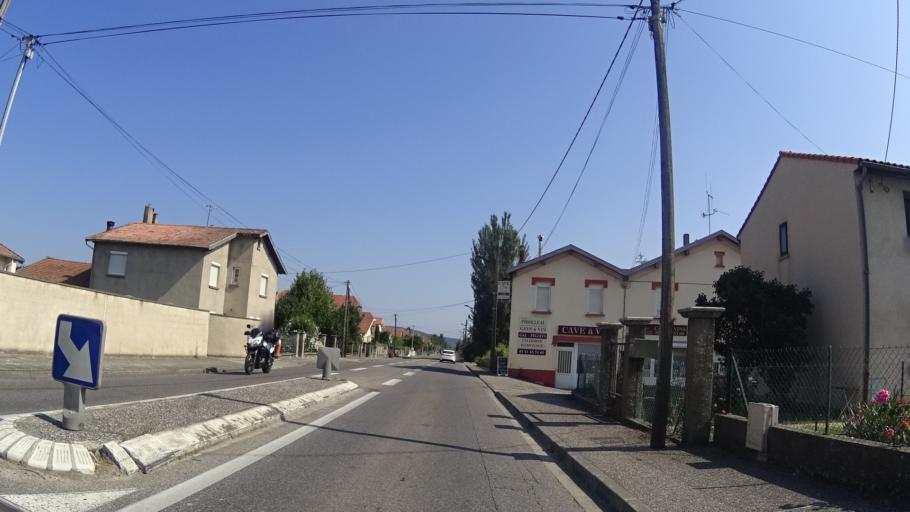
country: FR
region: Midi-Pyrenees
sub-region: Departement de l'Ariege
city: Lavelanet
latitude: 42.9652
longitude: 1.8651
